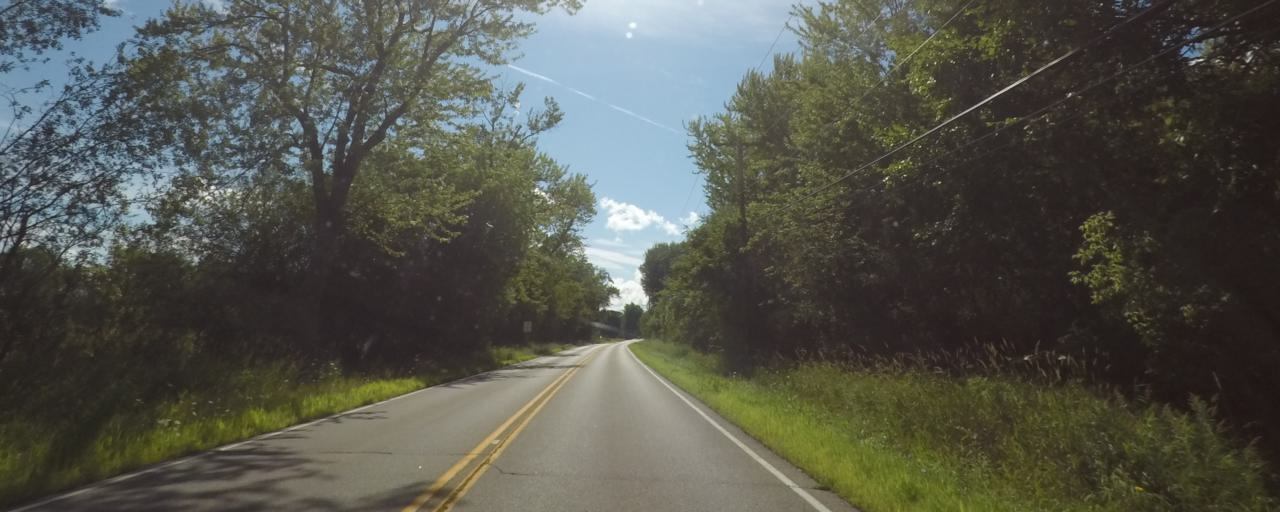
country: US
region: Wisconsin
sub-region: Waukesha County
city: Oconomowoc
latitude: 43.0844
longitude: -88.5080
